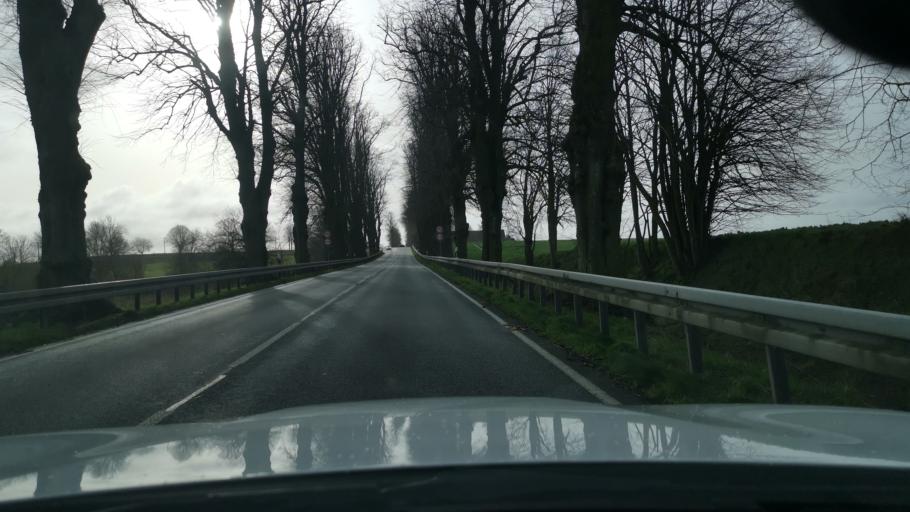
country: DE
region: Mecklenburg-Vorpommern
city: Laage
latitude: 53.9607
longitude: 12.2962
